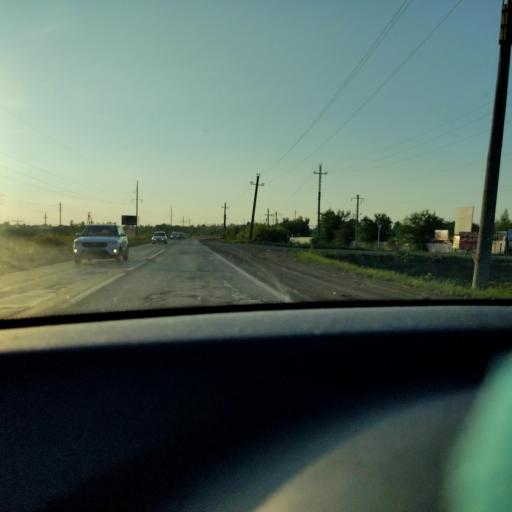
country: RU
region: Samara
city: Kinel'
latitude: 53.2356
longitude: 50.5829
